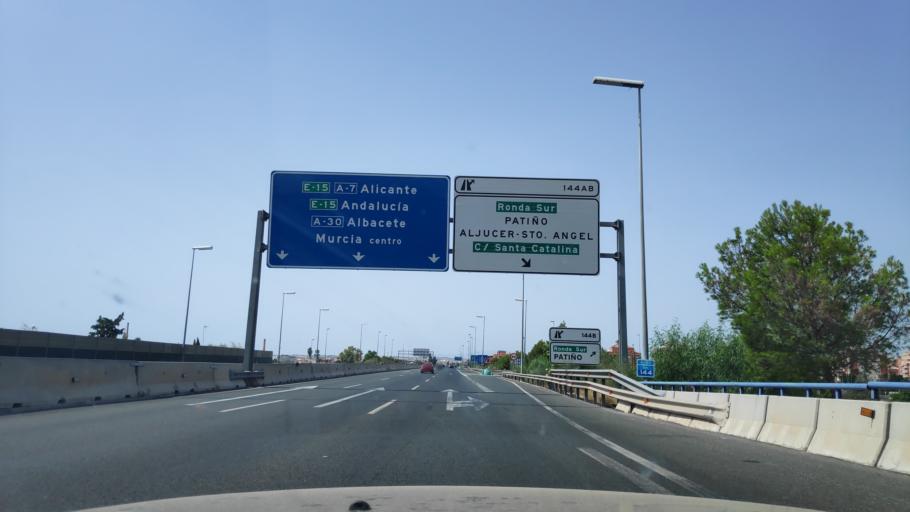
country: ES
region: Murcia
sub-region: Murcia
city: Murcia
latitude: 37.9641
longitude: -1.1357
